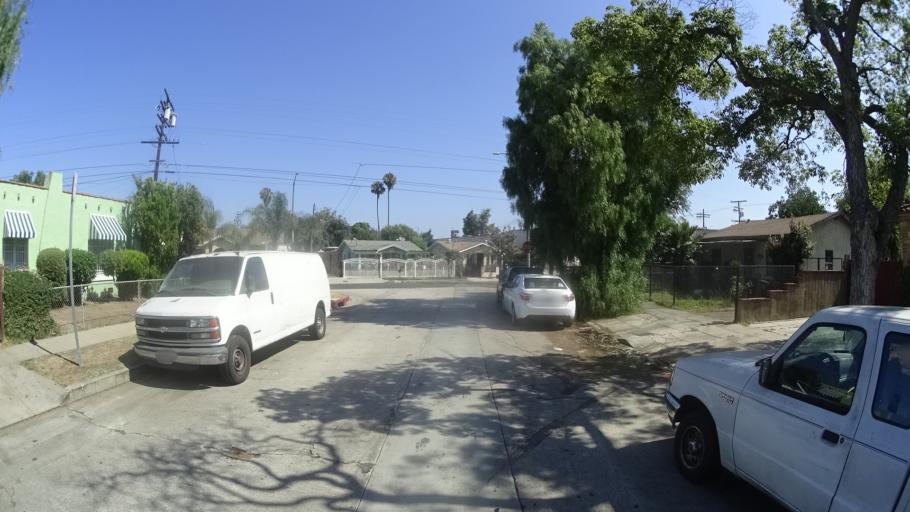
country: US
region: California
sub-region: Los Angeles County
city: View Park-Windsor Hills
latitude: 33.9807
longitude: -118.3226
